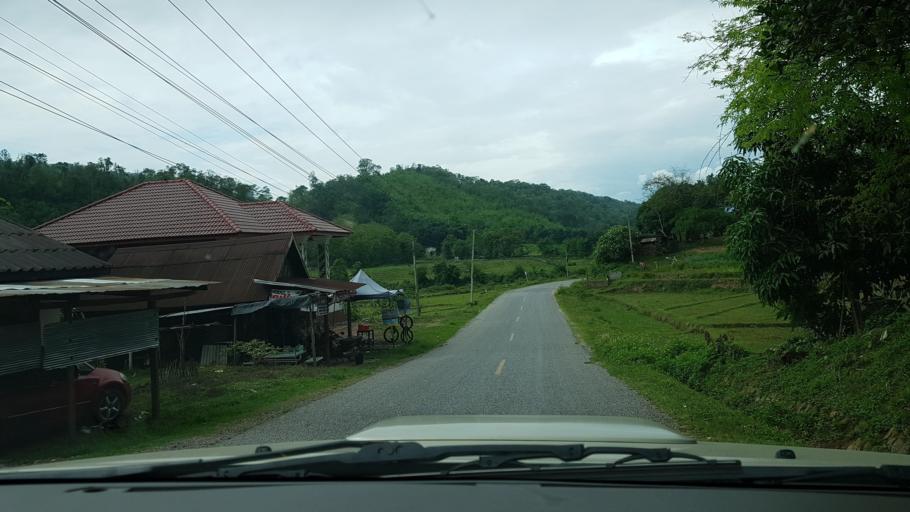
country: LA
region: Loungnamtha
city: Muang Nale
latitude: 20.3846
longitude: 101.7416
